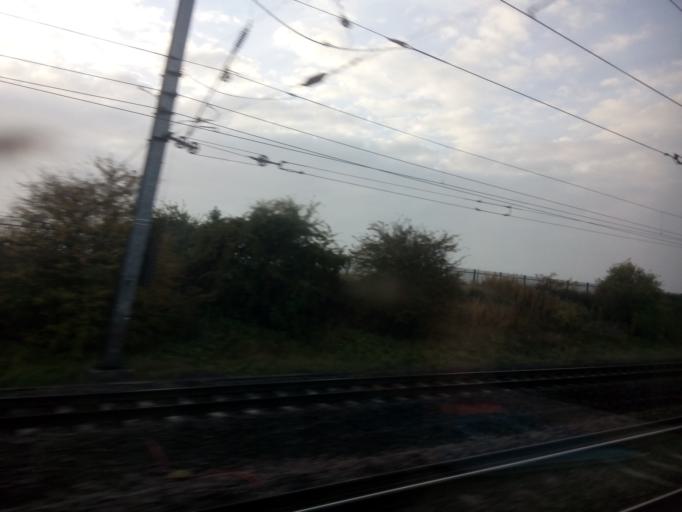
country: GB
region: England
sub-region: City of York
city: Copmanthorpe
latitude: 53.9085
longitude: -1.1430
